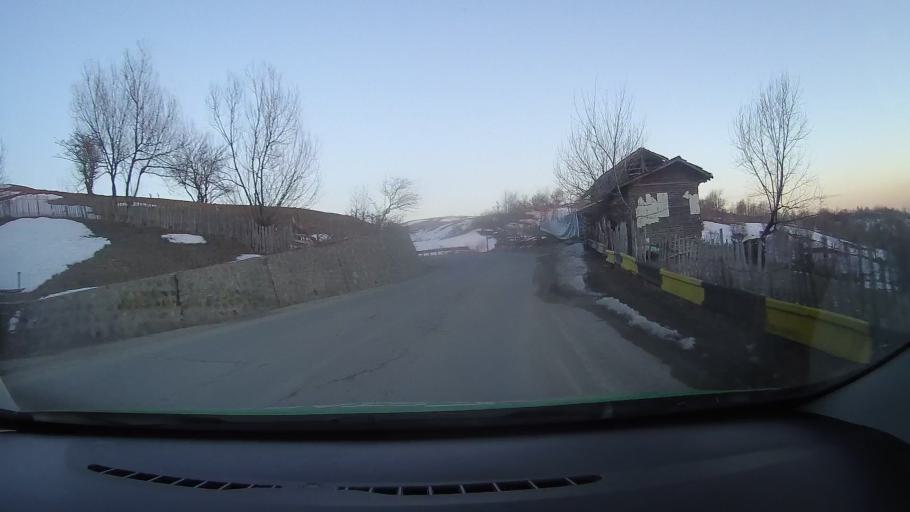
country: RO
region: Prahova
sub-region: Comuna Comarnic
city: Poiana
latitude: 45.2648
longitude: 25.6699
